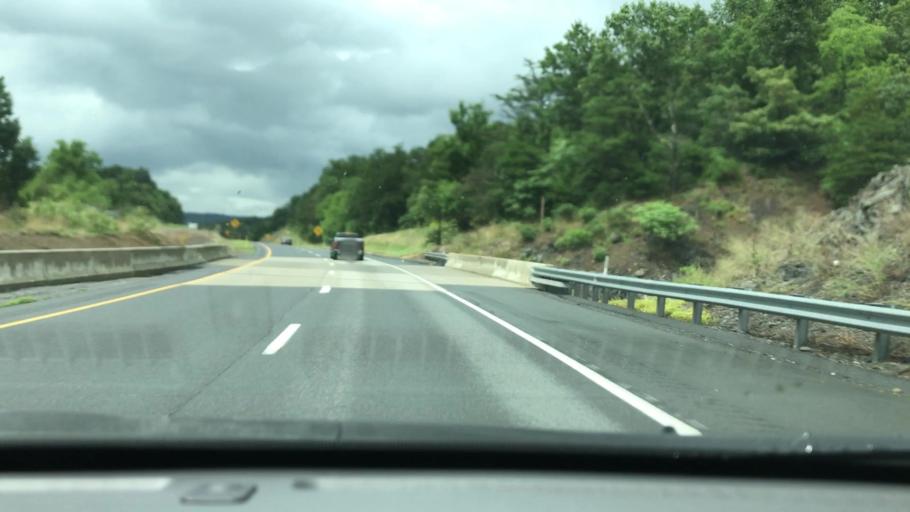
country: US
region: Maryland
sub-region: Washington County
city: Hancock
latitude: 39.7756
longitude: -78.2002
